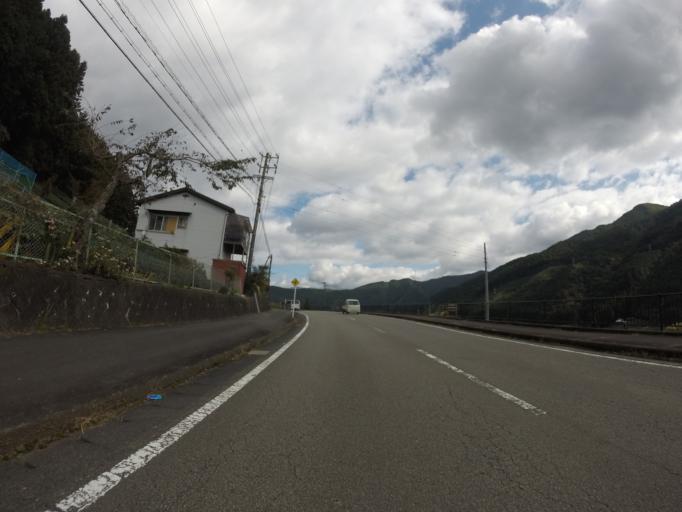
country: JP
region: Shizuoka
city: Kanaya
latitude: 35.0653
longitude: 138.1036
